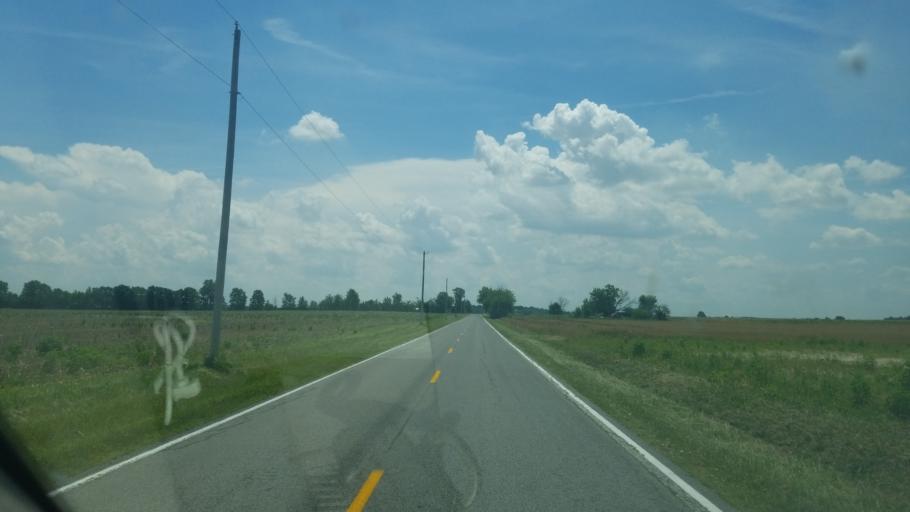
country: US
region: Ohio
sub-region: Hancock County
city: Arlington
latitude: 40.9032
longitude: -83.5947
